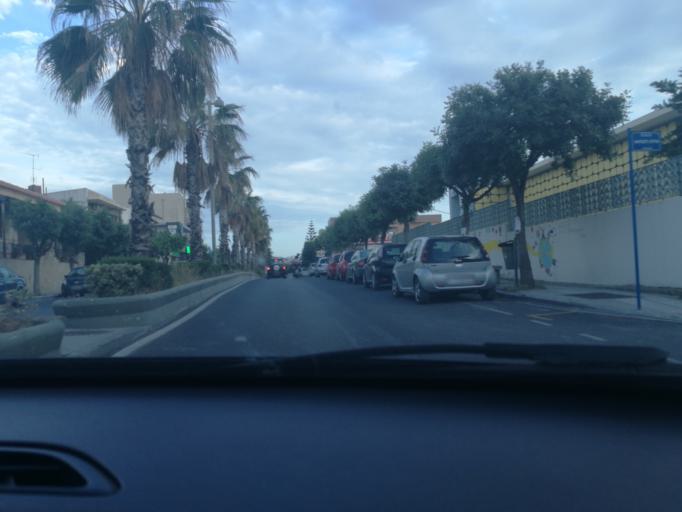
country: GR
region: Crete
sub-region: Nomos Irakleiou
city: Irakleion
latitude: 35.3169
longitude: 25.1458
